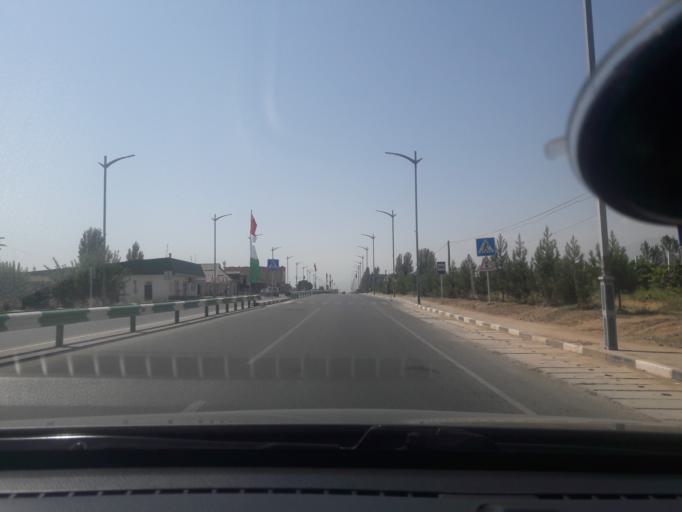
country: TJ
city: Shahrinav
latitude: 38.5620
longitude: 68.4235
